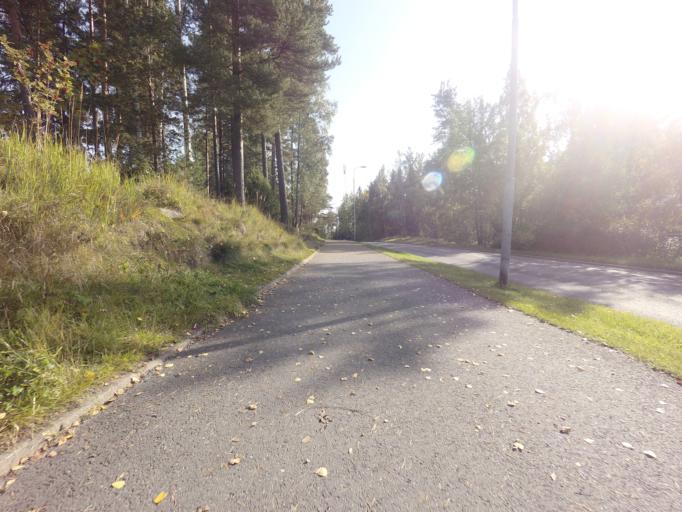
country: FI
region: Uusimaa
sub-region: Helsinki
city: Espoo
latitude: 60.1728
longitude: 24.6557
